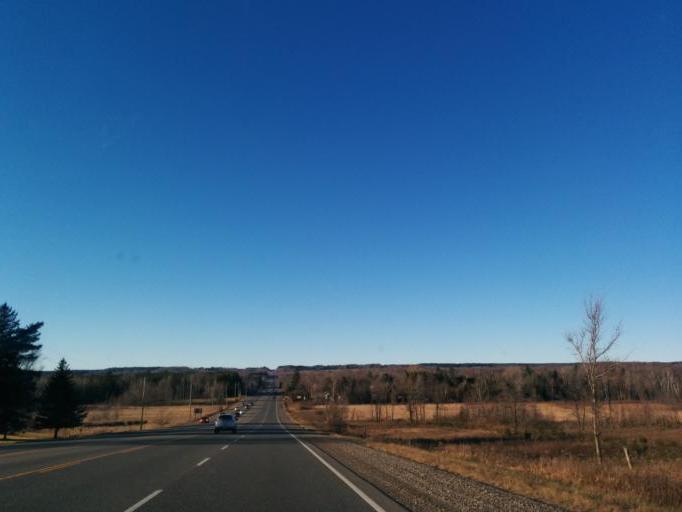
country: CA
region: Ontario
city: Orangeville
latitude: 43.8173
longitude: -79.9377
